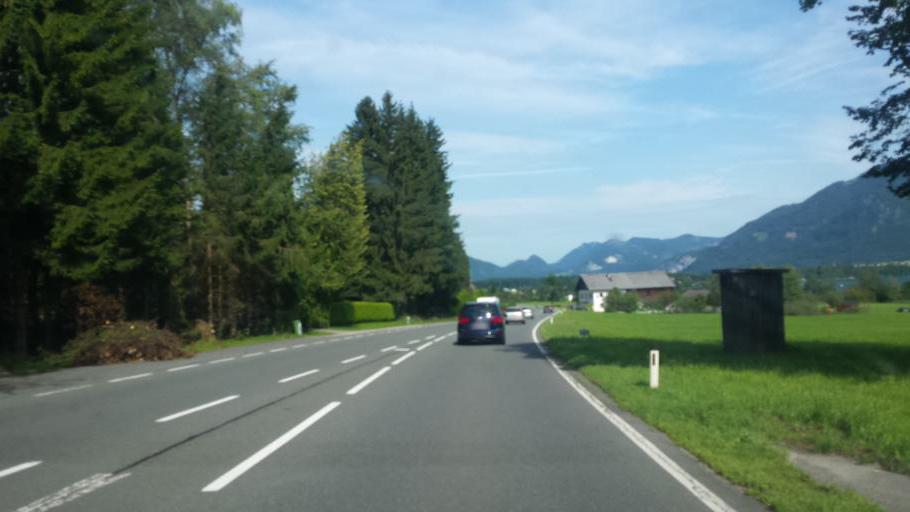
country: AT
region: Upper Austria
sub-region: Politischer Bezirk Gmunden
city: Sankt Wolfgang im Salzkammergut
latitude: 47.7121
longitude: 13.4525
